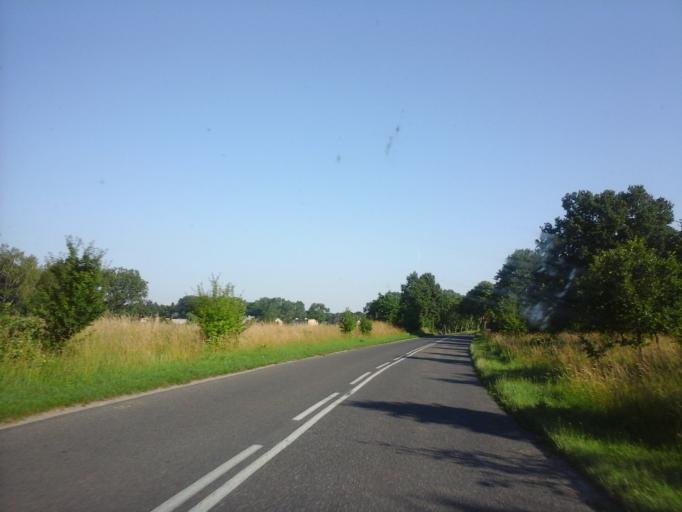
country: PL
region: West Pomeranian Voivodeship
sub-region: Powiat stargardzki
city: Chociwel
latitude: 53.4417
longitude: 15.3522
